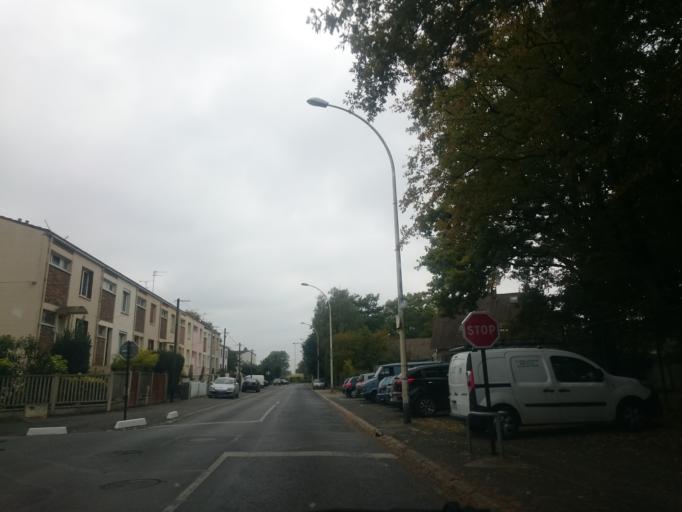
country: FR
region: Ile-de-France
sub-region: Departement de l'Essonne
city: Morsang-sur-Orge
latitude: 48.6474
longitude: 2.3462
